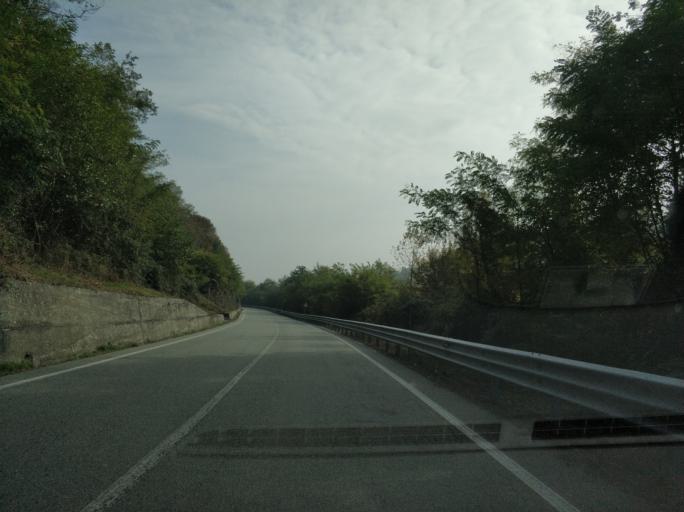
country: IT
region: Piedmont
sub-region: Provincia di Biella
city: Sala Biellese
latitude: 45.5184
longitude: 7.9587
